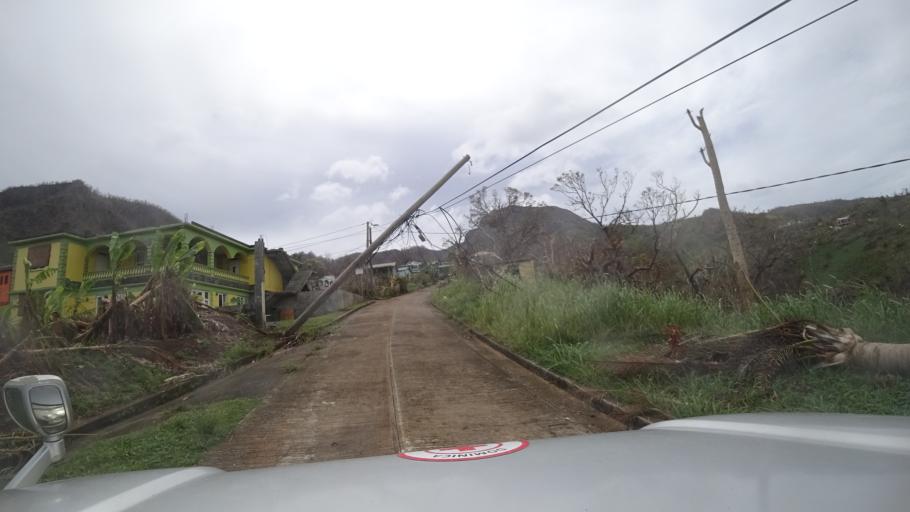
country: DM
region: Saint John
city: Portsmouth
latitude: 15.6132
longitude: -61.4112
